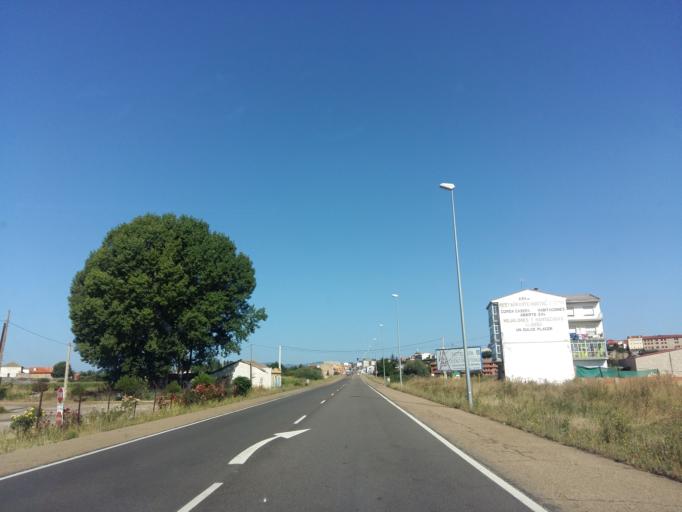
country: ES
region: Castille and Leon
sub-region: Provincia de Leon
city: Astorga
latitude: 42.4474
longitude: -6.0484
